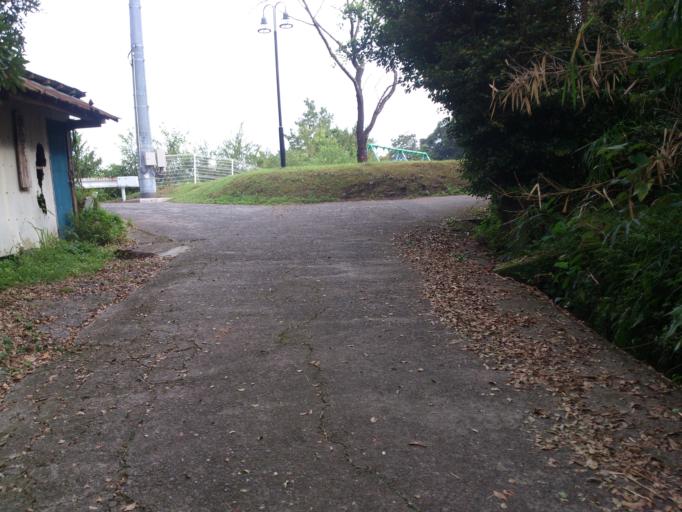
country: JP
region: Kagoshima
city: Kanoya
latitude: 31.3467
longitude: 130.9545
